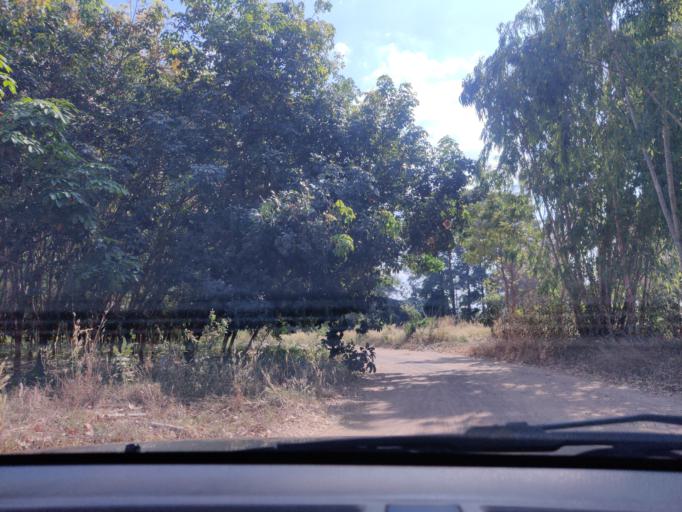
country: TH
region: Sisaket
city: Si Sa Ket
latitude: 15.0793
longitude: 104.3507
